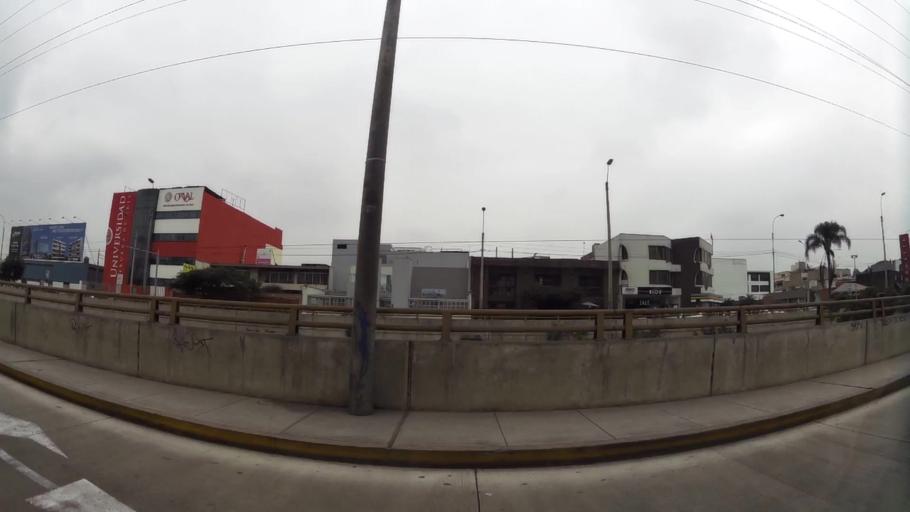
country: PE
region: Lima
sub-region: Lima
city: Surco
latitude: -12.1113
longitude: -76.9909
